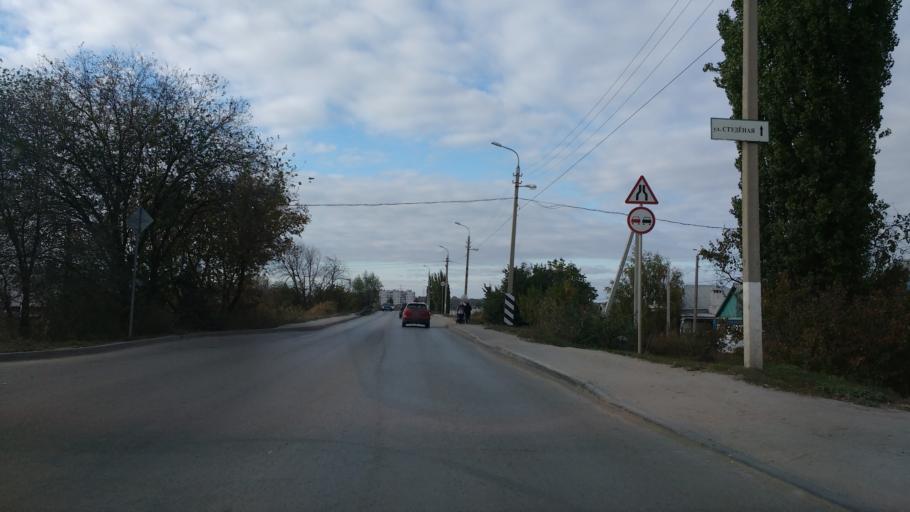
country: RU
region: Volgograd
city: Volgograd
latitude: 48.7686
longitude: 44.5268
